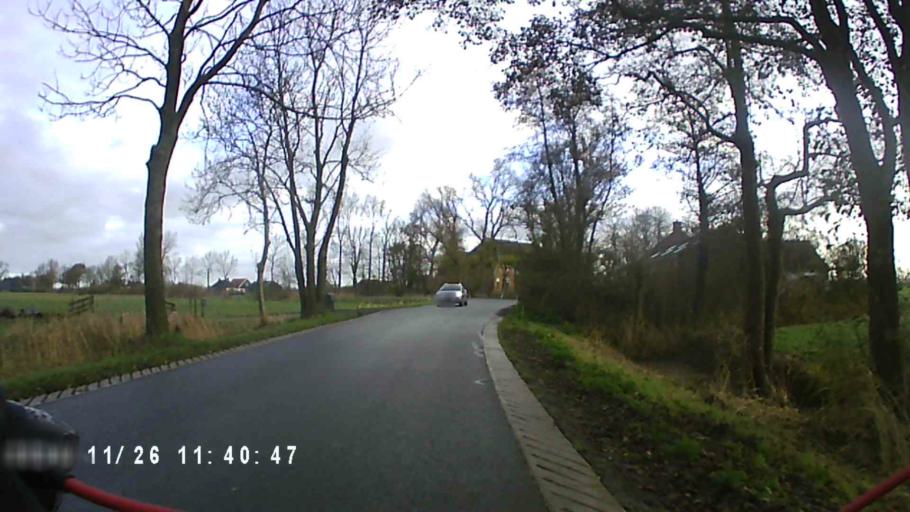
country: NL
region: Groningen
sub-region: Gemeente Bedum
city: Bedum
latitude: 53.2888
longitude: 6.5700
